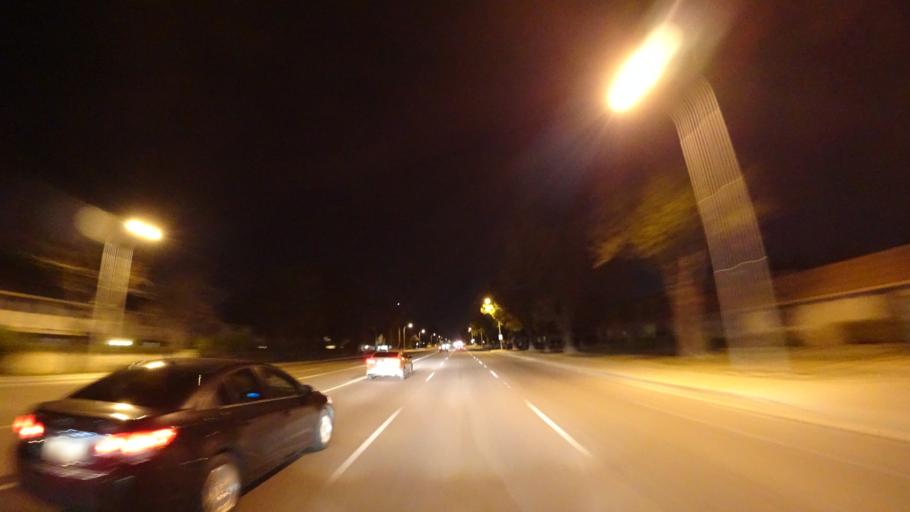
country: US
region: Arizona
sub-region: Maricopa County
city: Tempe
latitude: 33.3785
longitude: -111.9113
